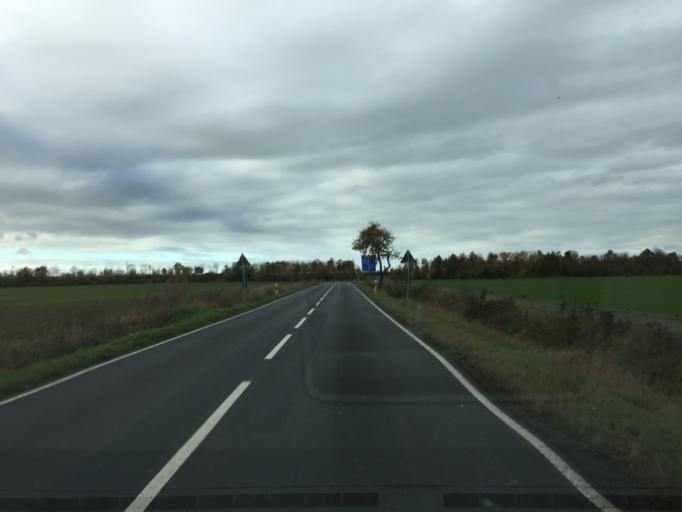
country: DE
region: Lower Saxony
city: Leiferde
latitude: 52.1756
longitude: 10.5124
